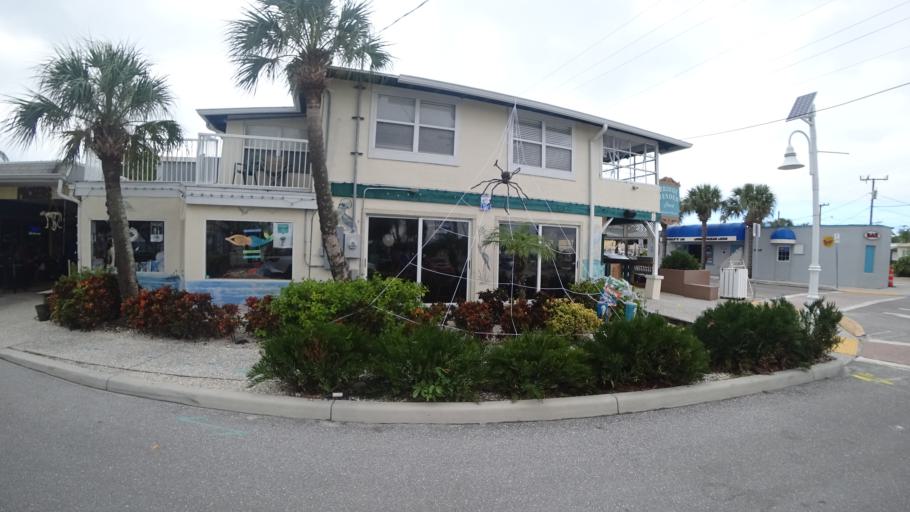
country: US
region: Florida
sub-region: Manatee County
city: Bradenton Beach
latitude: 27.4653
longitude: -82.6966
